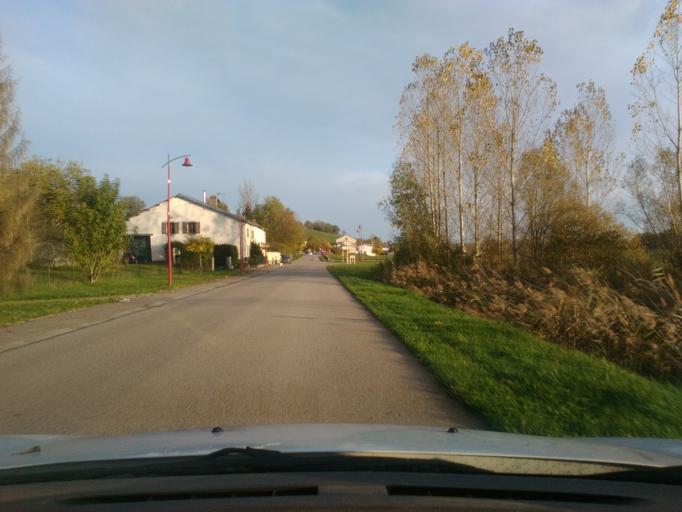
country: FR
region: Lorraine
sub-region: Departement des Vosges
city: Mirecourt
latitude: 48.2640
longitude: 6.1681
